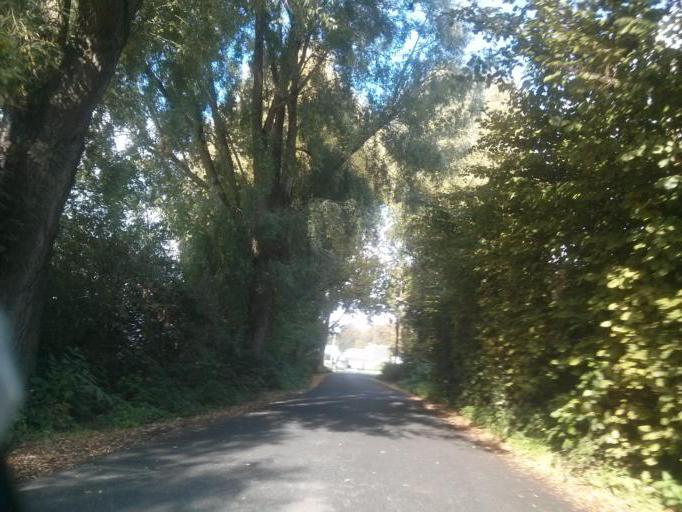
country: DE
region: North Rhine-Westphalia
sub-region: Regierungsbezirk Koln
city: Poll
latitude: 50.9086
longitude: 6.9871
